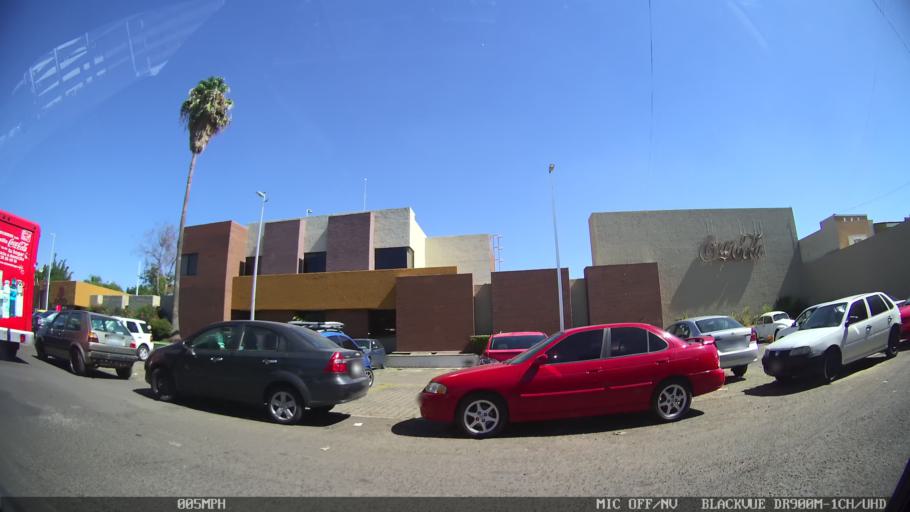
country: MX
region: Jalisco
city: Tlaquepaque
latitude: 20.6513
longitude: -103.2915
